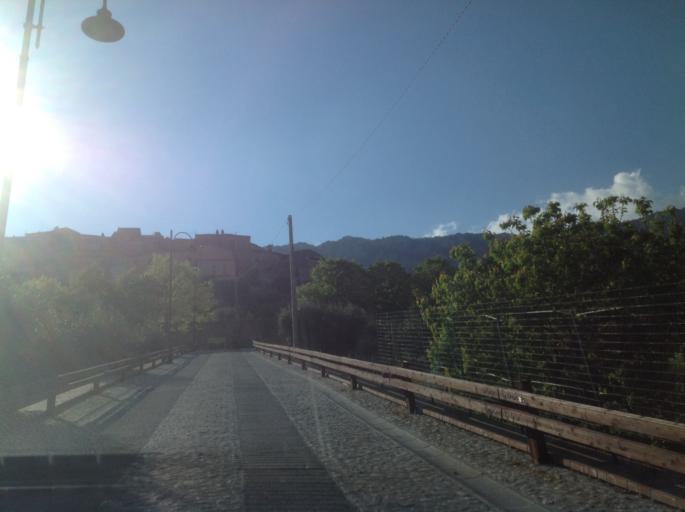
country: IT
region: Calabria
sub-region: Provincia di Cosenza
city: Civita
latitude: 39.8295
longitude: 16.3138
